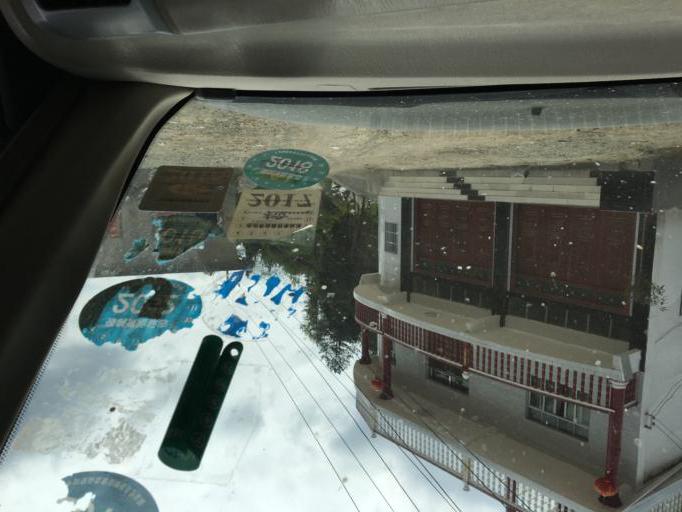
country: CN
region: Guizhou Sheng
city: Kuanping
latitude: 28.0244
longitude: 108.0667
